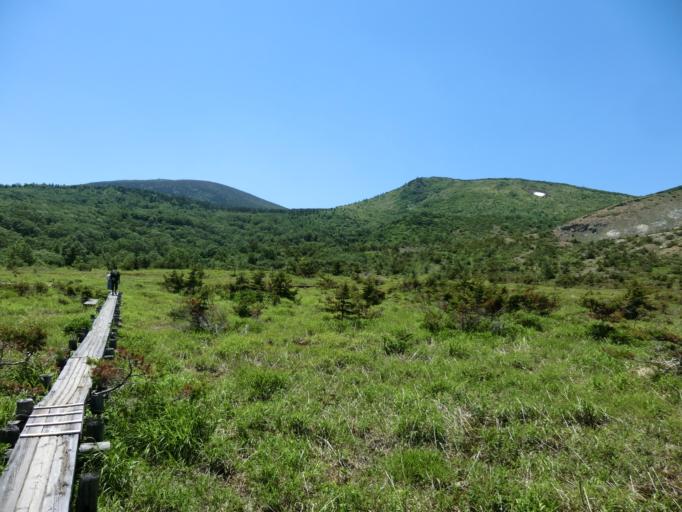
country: JP
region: Fukushima
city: Inawashiro
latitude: 37.7215
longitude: 140.2531
